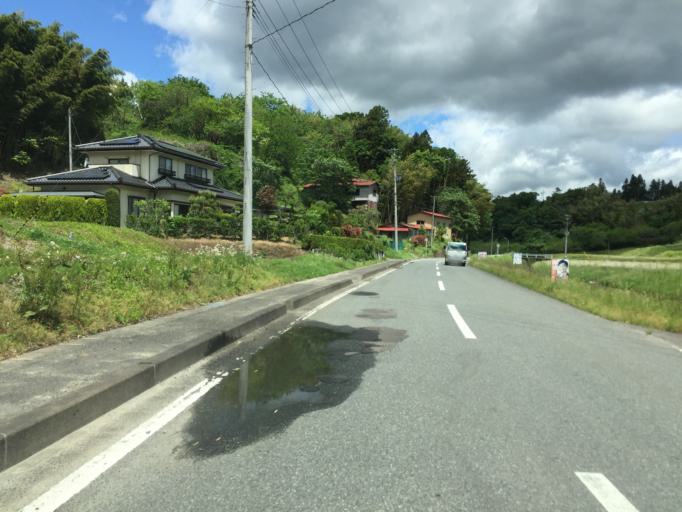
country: JP
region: Fukushima
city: Nihommatsu
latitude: 37.5441
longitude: 140.4701
